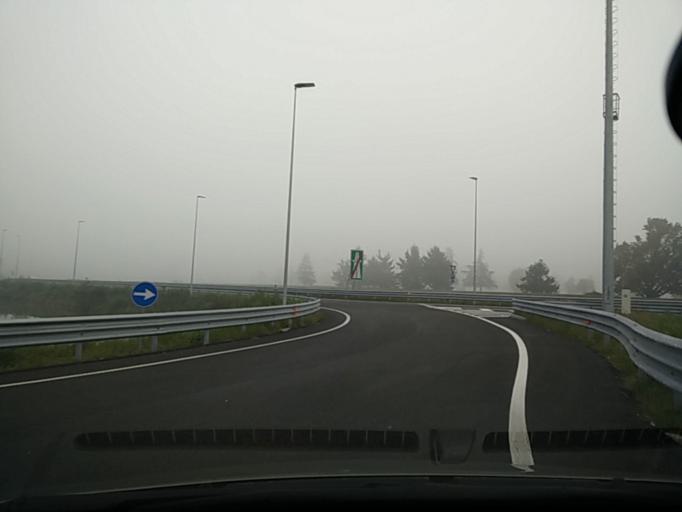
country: IT
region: Veneto
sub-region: Provincia di Venezia
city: Martellago
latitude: 45.5580
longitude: 12.1559
